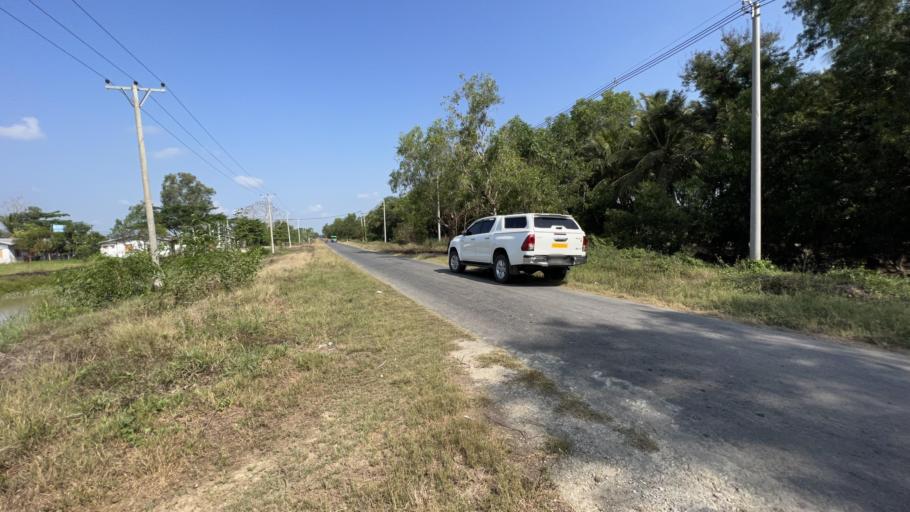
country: MM
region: Ayeyarwady
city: Kyaiklat
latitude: 16.4003
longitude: 95.8495
